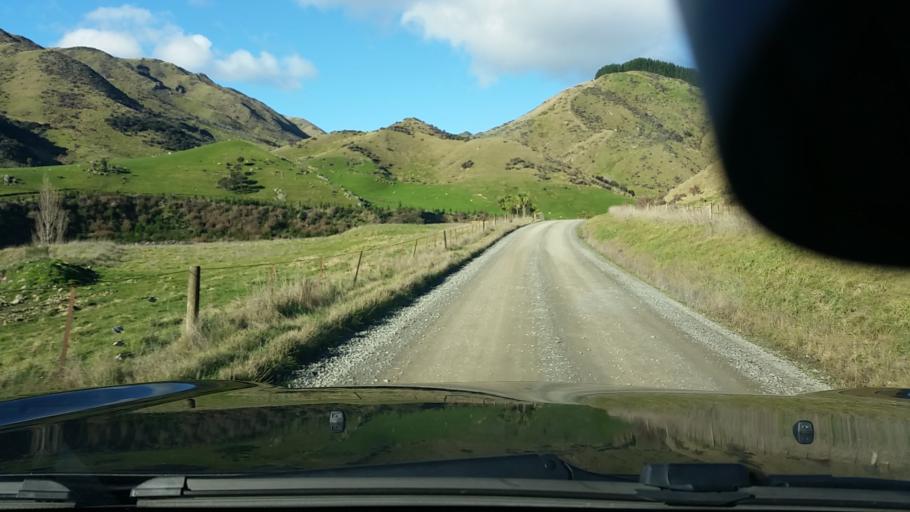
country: NZ
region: Marlborough
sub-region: Marlborough District
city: Blenheim
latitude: -41.6031
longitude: 173.9714
